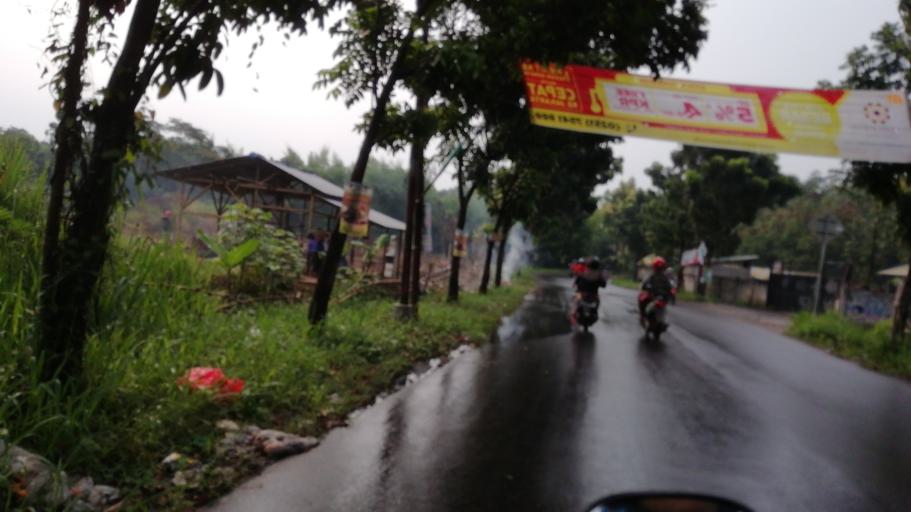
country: ID
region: West Java
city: Bogor
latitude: -6.5317
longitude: 106.8066
